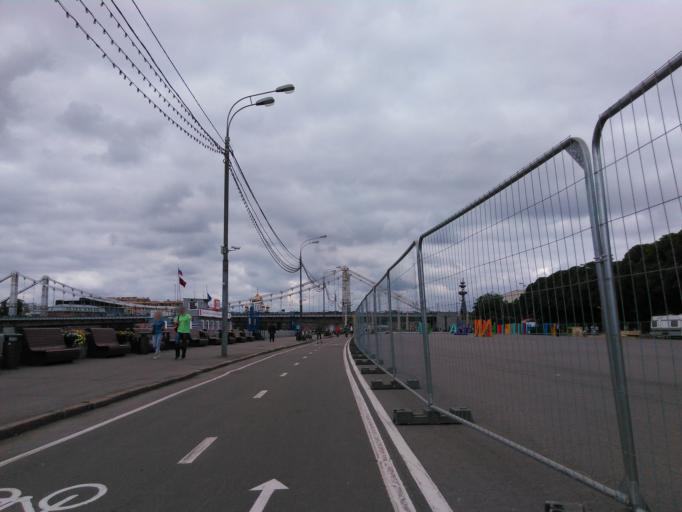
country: RU
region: Moscow
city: Moscow
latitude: 55.7312
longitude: 37.5982
